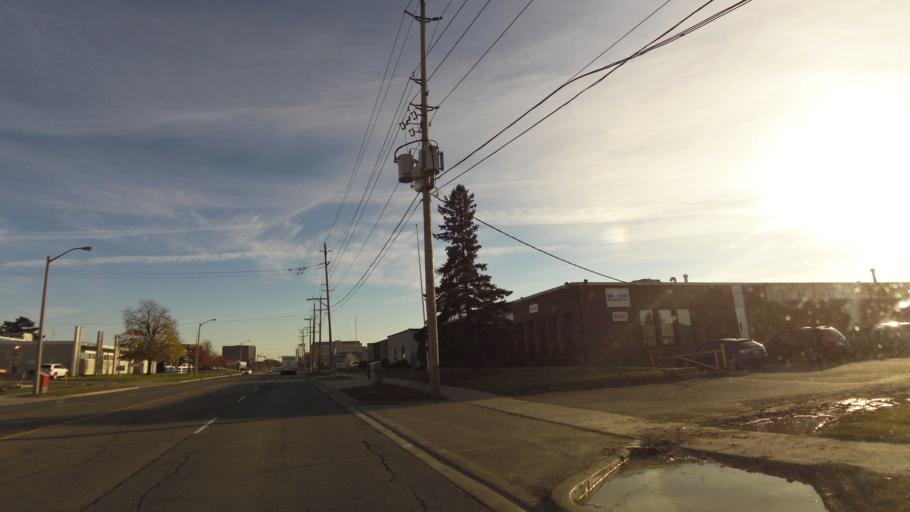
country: CA
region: Ontario
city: Etobicoke
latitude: 43.6957
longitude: -79.5896
